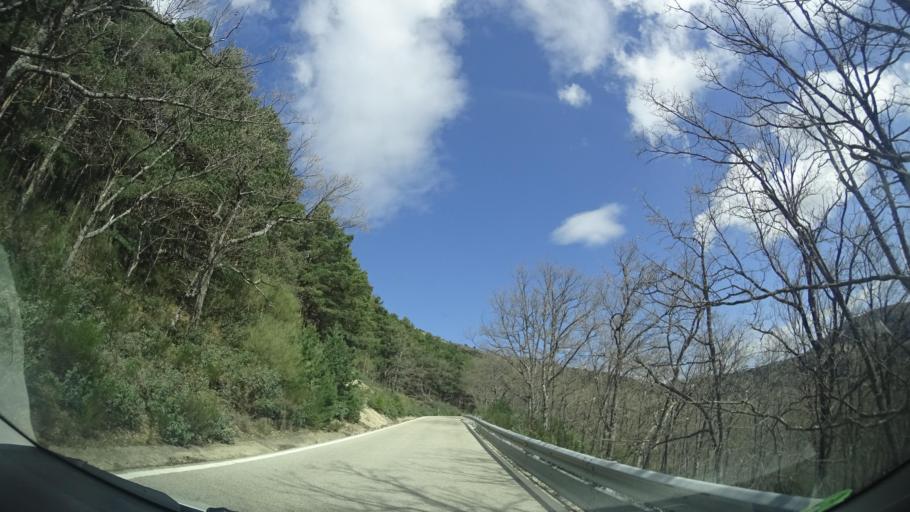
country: ES
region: Madrid
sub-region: Provincia de Madrid
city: Miraflores de la Sierra
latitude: 40.8503
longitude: -3.7658
